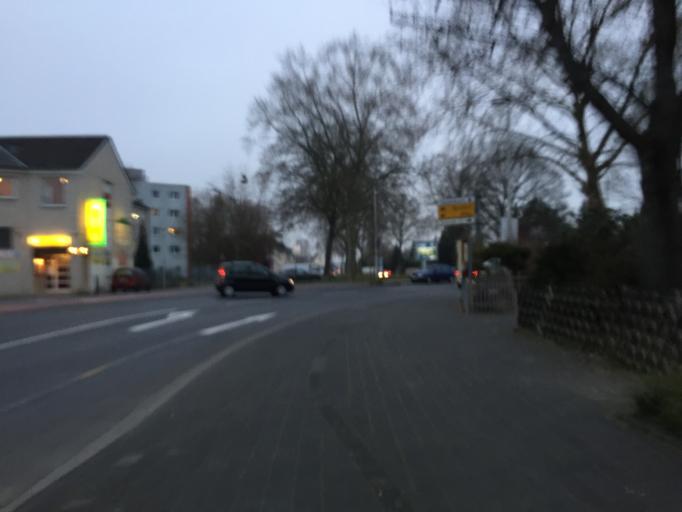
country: DE
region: North Rhine-Westphalia
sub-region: Regierungsbezirk Koln
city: Alfter
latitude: 50.7393
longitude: 7.0468
